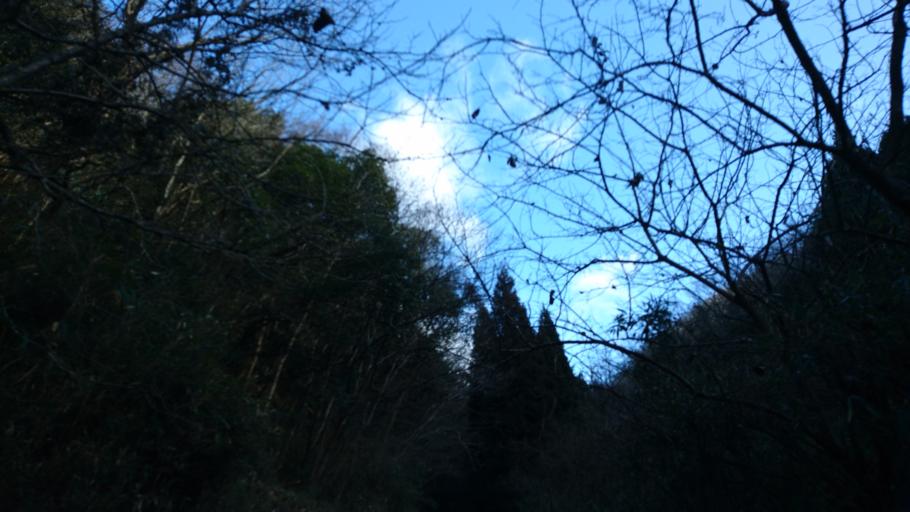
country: JP
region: Okayama
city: Takahashi
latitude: 34.8629
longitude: 133.5660
